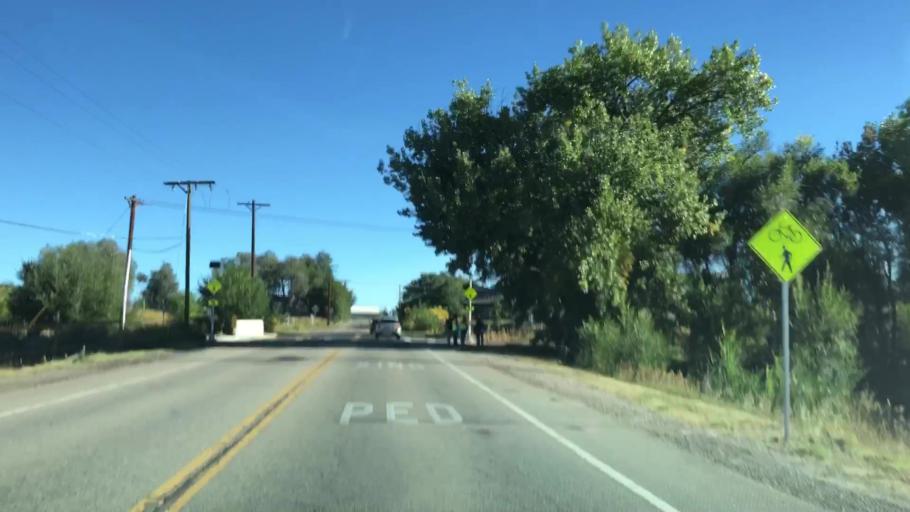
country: US
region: Colorado
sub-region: Larimer County
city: Loveland
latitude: 40.4052
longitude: -105.1216
